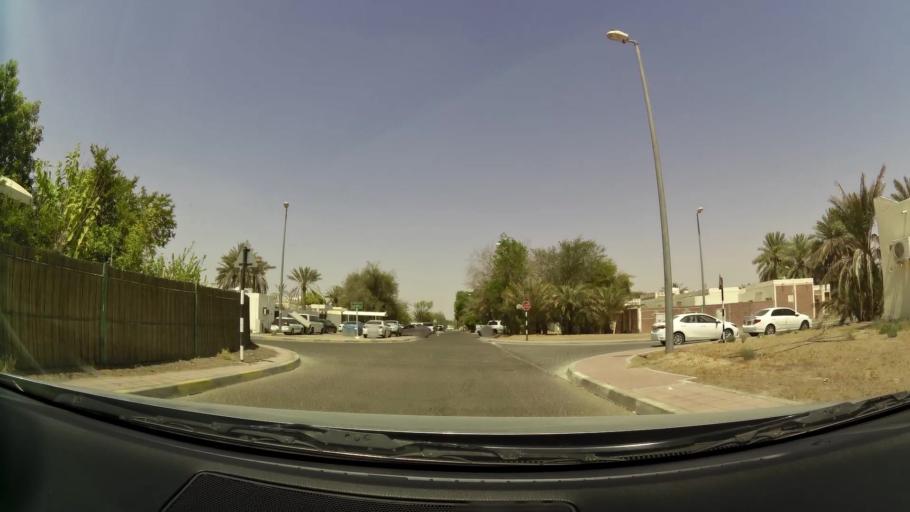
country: OM
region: Al Buraimi
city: Al Buraymi
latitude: 24.2771
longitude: 55.7747
